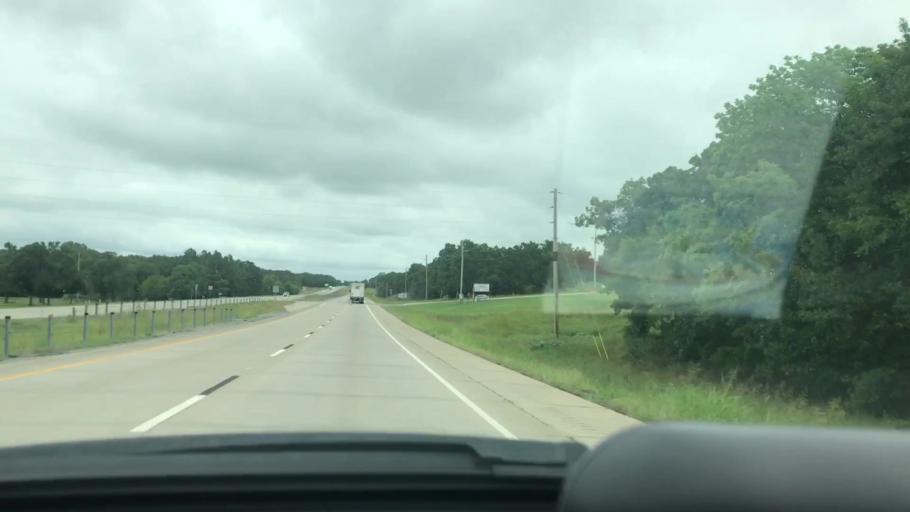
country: US
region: Oklahoma
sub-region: Pittsburg County
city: McAlester
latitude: 34.7018
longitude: -95.9077
